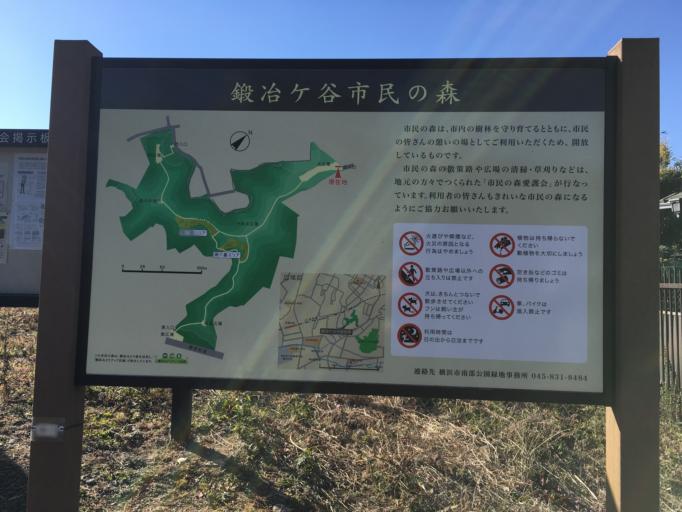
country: JP
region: Kanagawa
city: Kamakura
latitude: 35.3705
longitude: 139.5616
